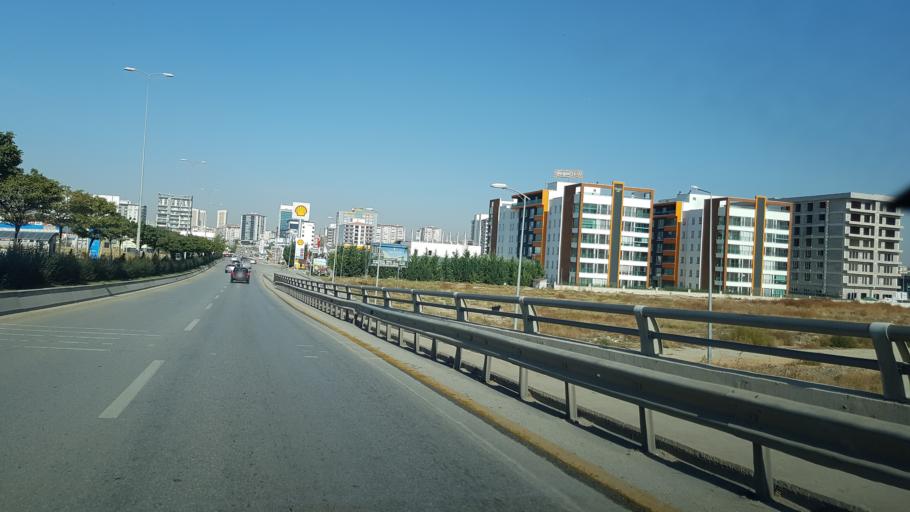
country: TR
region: Ankara
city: Etimesgut
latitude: 39.9613
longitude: 32.6060
